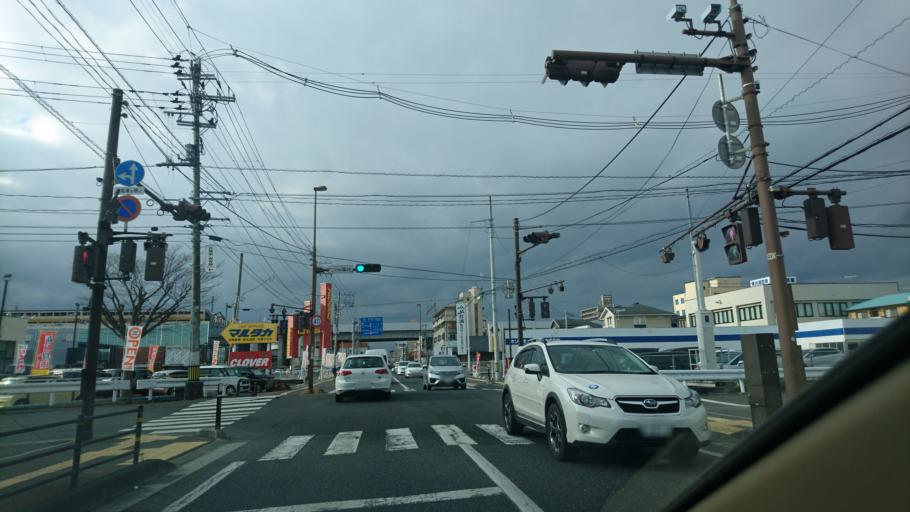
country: JP
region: Miyagi
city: Furukawa
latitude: 38.5725
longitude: 140.9709
